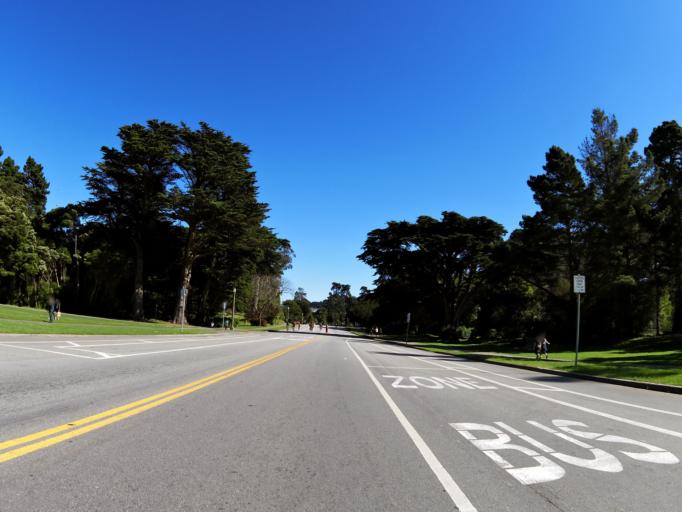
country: US
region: California
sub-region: San Francisco County
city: San Francisco
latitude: 37.7713
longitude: -122.4590
